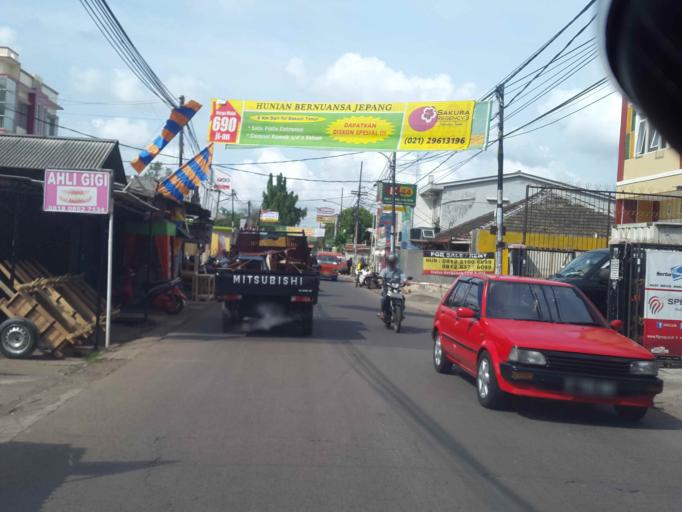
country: ID
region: West Java
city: Bekasi
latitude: -6.3027
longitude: 106.9237
